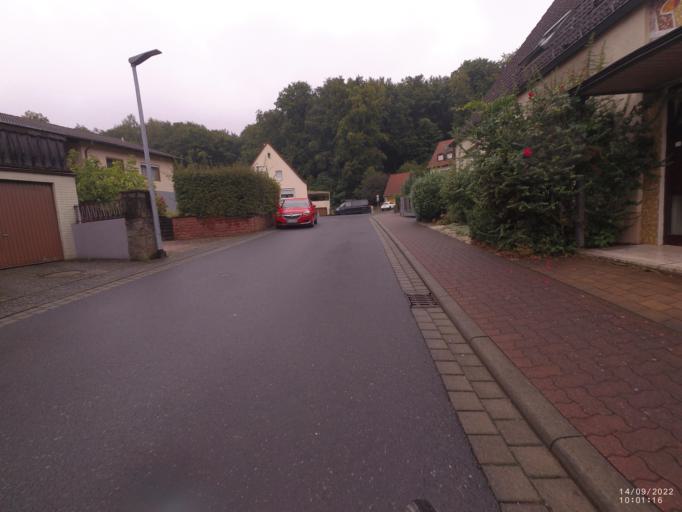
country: DE
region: Bavaria
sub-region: Regierungsbezirk Unterfranken
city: Glattbach
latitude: 50.0105
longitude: 9.1529
